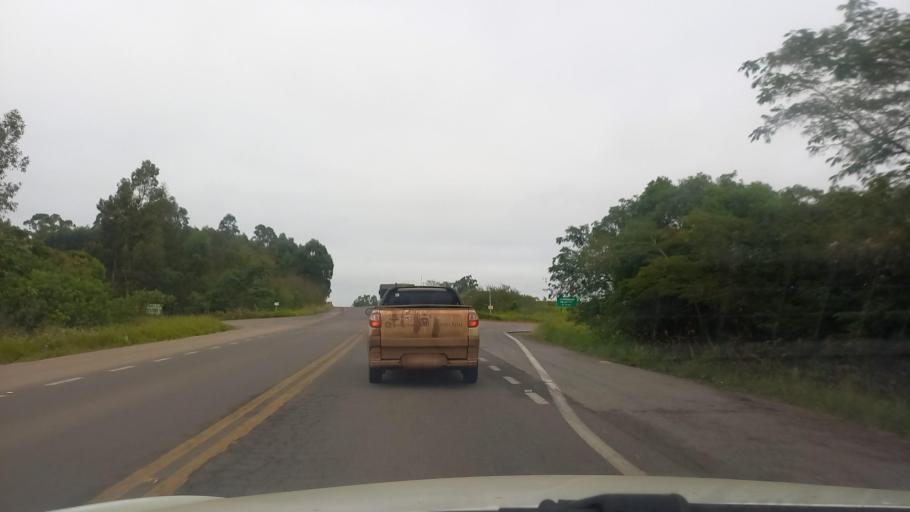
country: BR
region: Rio Grande do Sul
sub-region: Sao Pedro Do Sul
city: Sao Pedro do Sul
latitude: -29.7715
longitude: -54.0949
